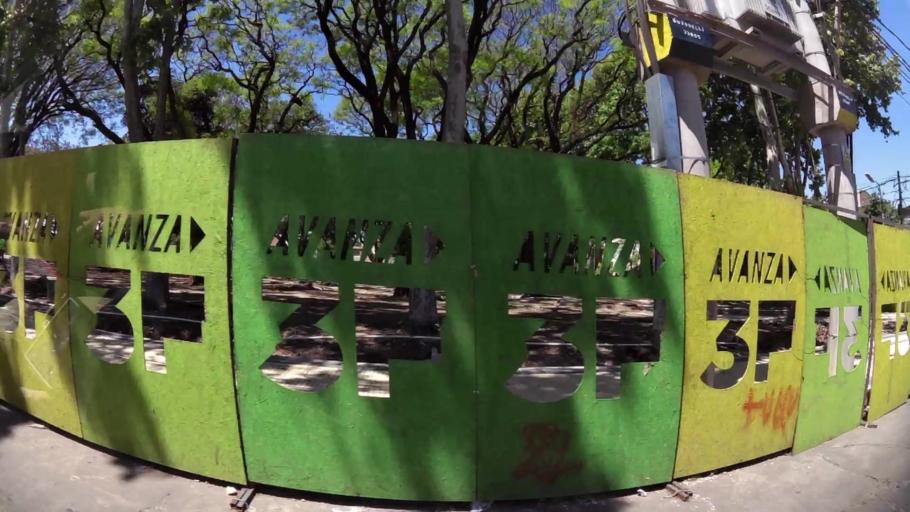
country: AR
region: Buenos Aires
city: Caseros
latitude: -34.6025
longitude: -58.5520
